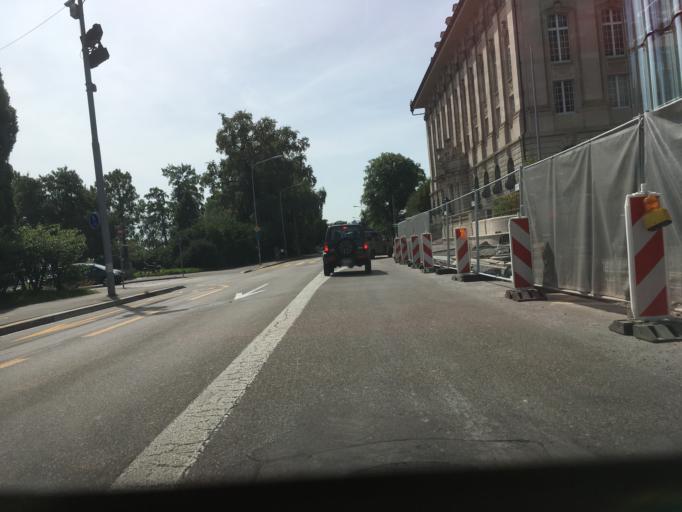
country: CH
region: Zurich
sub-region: Bezirk Zuerich
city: Zuerich (Kreis 2) / Enge
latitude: 47.3599
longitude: 8.5354
